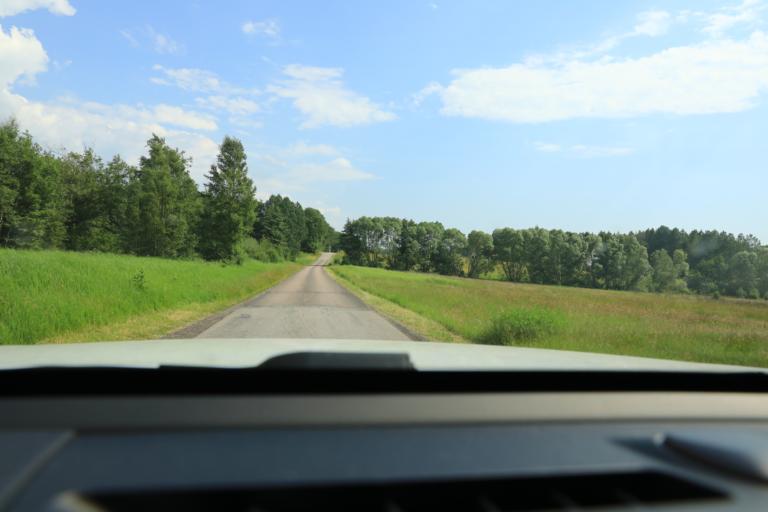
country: SE
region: Halland
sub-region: Varbergs Kommun
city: Varberg
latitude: 57.1560
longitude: 12.3180
